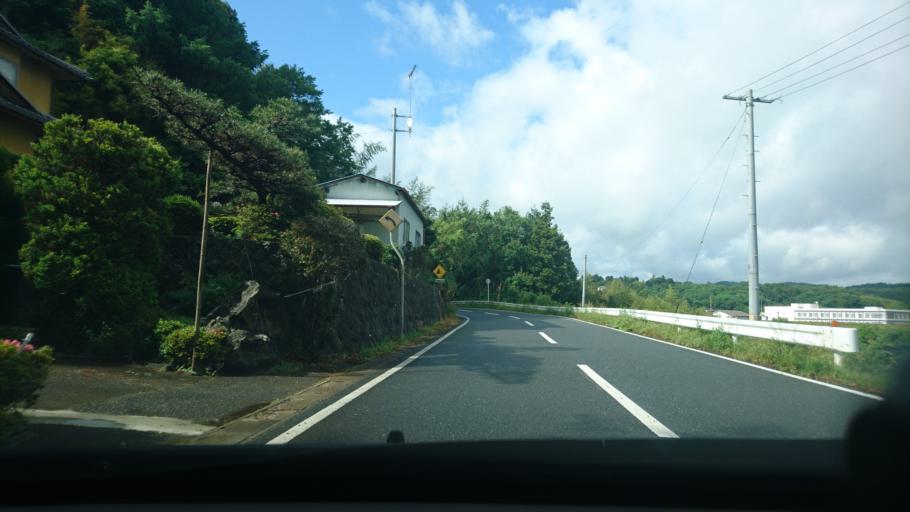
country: JP
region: Miyagi
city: Wakuya
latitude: 38.7023
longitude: 141.2858
